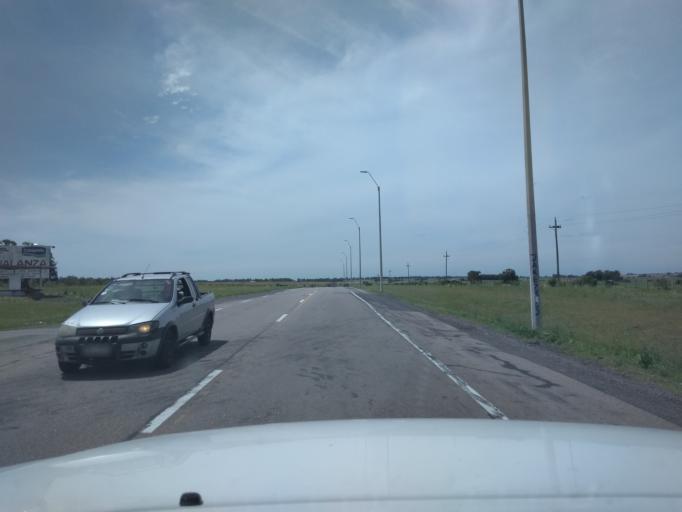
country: UY
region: Florida
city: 25 de Mayo
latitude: -34.2378
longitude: -56.2132
